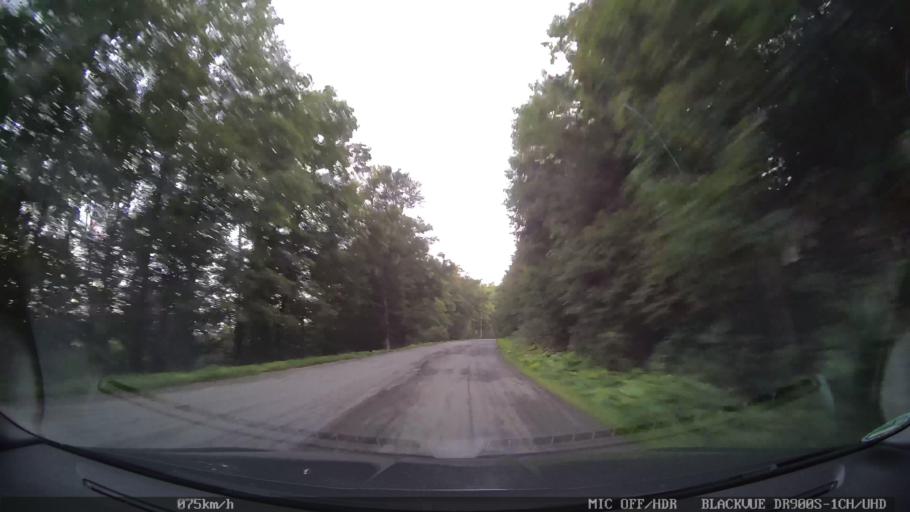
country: HR
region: Primorsko-Goranska
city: Novi Vinodolski
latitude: 45.1763
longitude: 14.9851
